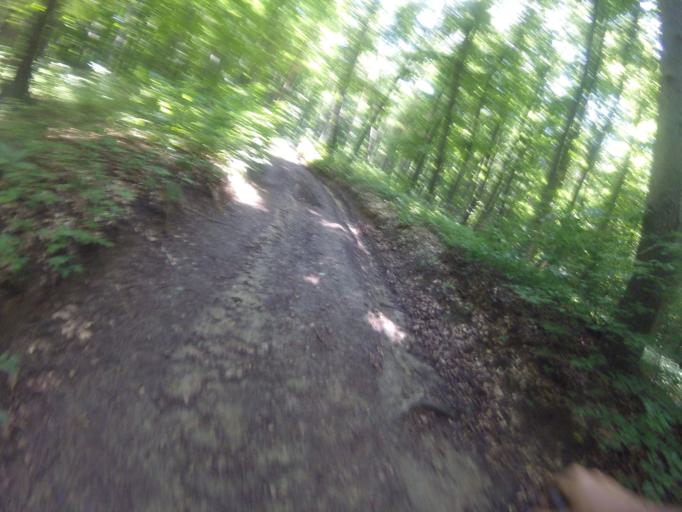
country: HU
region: Veszprem
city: Cseteny
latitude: 47.2626
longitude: 18.0029
